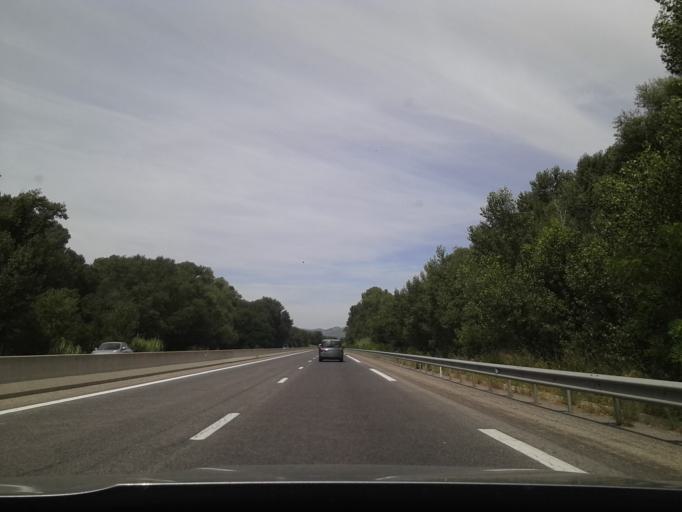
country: FR
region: Languedoc-Roussillon
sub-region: Departement des Pyrenees-Orientales
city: Corneilla-la-Riviere
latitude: 42.6848
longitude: 2.7422
